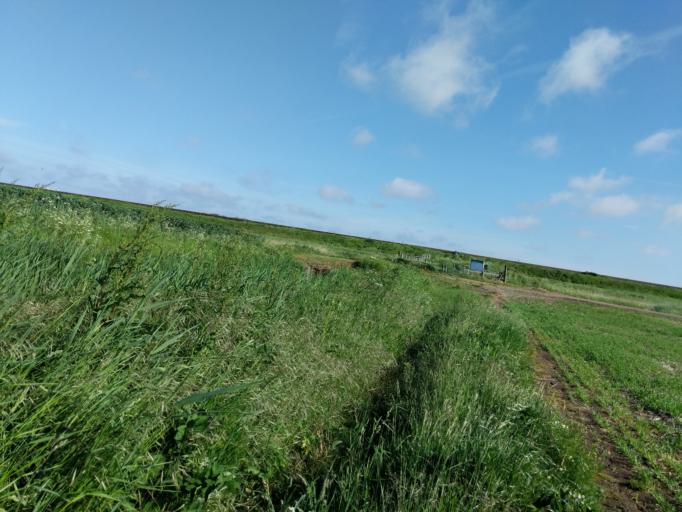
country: GB
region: England
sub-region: Kent
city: Faversham
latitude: 51.3425
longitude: 0.9190
